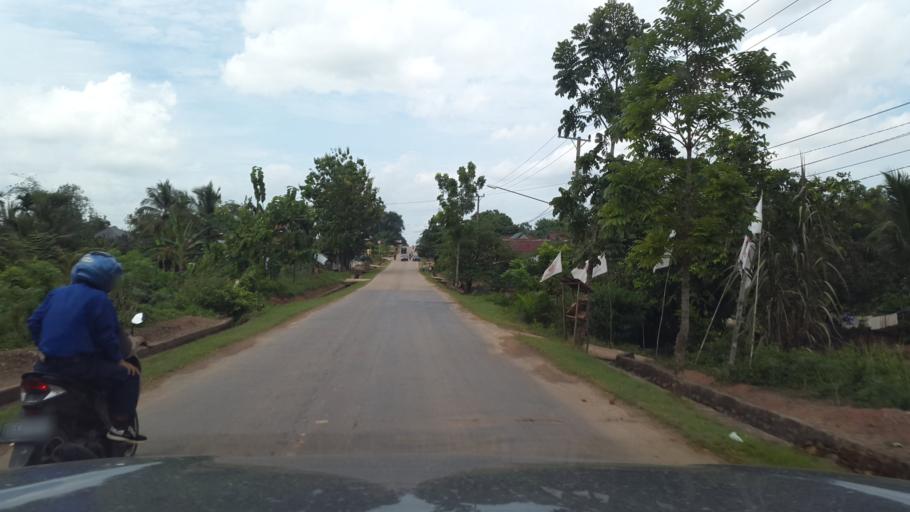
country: ID
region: South Sumatra
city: Gunungmegang Dalam
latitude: -3.3034
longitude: 103.8622
